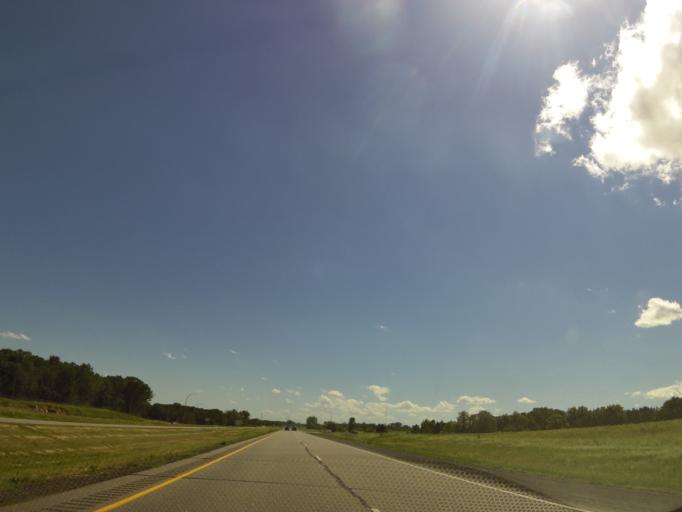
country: US
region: Minnesota
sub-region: Stearns County
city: Waite Park
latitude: 45.5148
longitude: -94.2268
